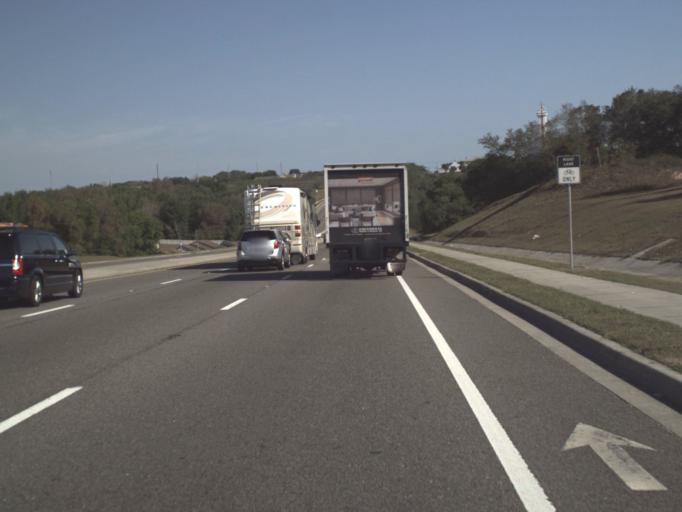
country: US
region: Florida
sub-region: Lake County
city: Minneola
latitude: 28.5551
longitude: -81.7427
